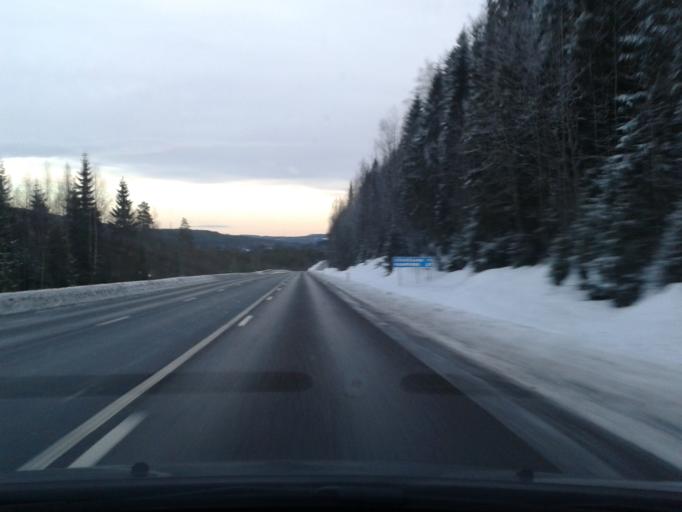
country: SE
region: Vaesternorrland
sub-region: Kramfors Kommun
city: Bollstabruk
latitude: 63.1124
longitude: 17.4991
